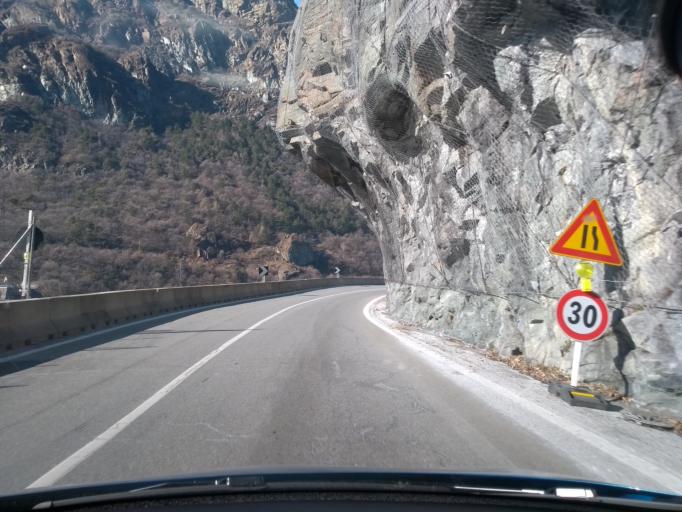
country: IT
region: Aosta Valley
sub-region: Valle d'Aosta
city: Montjovet
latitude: 45.7217
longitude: 7.6694
